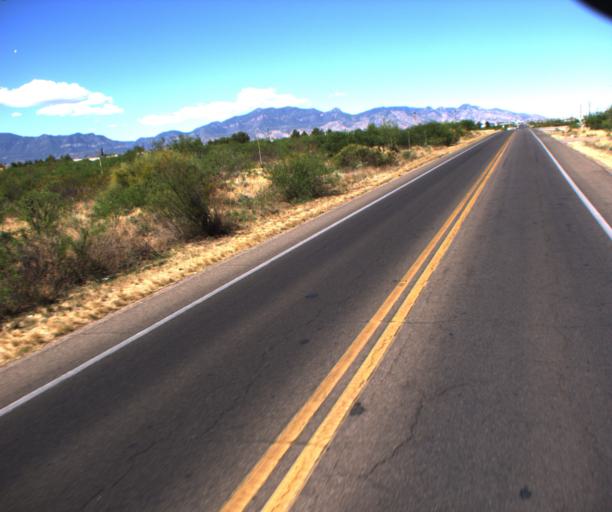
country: US
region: Arizona
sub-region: Cochise County
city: Sierra Vista
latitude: 31.5547
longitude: -110.2122
